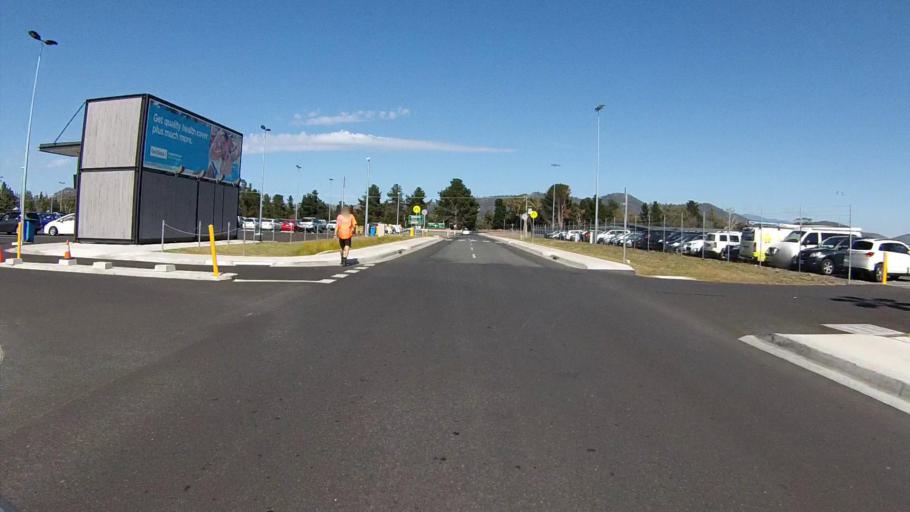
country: AU
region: Tasmania
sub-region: Clarence
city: Seven Mile Beach
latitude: -42.8401
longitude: 147.5046
